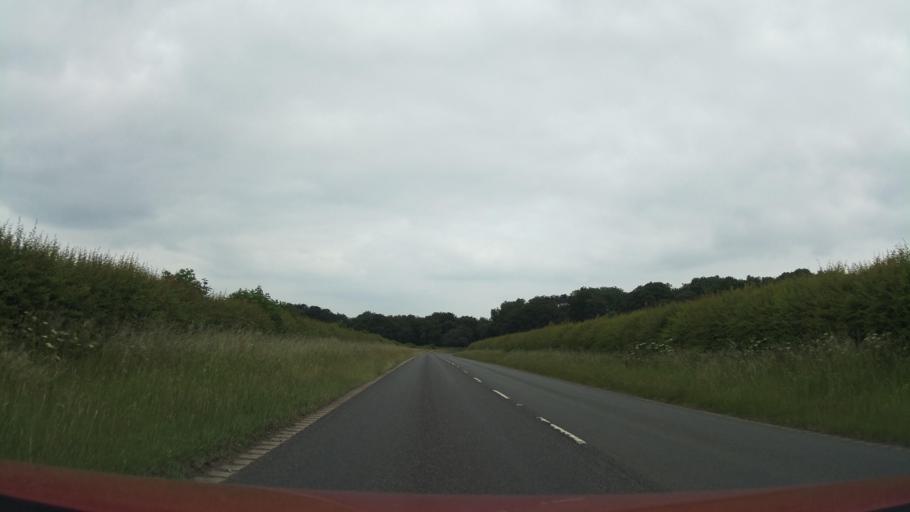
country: GB
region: England
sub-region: District of Rutland
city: Empingham
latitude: 52.6511
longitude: -0.6088
